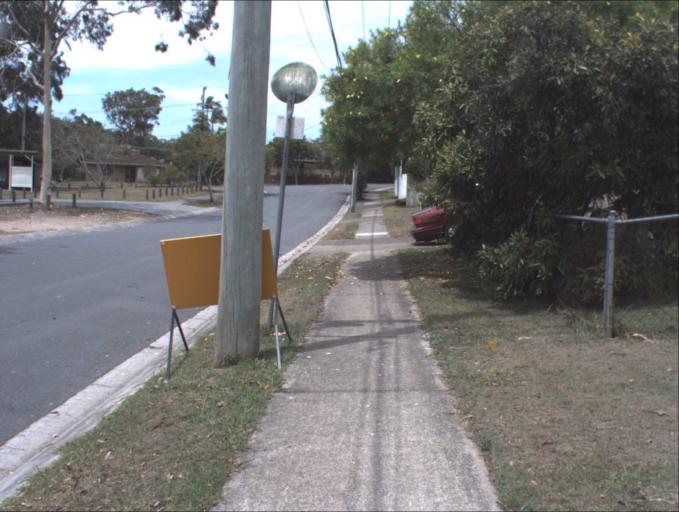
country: AU
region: Queensland
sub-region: Logan
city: Springwood
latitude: -27.6269
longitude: 153.1336
